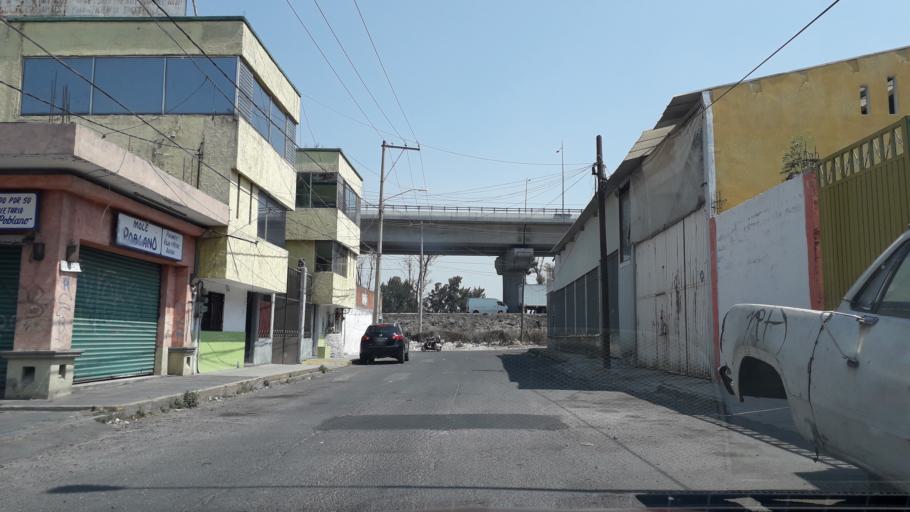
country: MX
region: Puebla
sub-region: Cuautlancingo
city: Sanctorum
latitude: 19.0879
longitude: -98.2136
